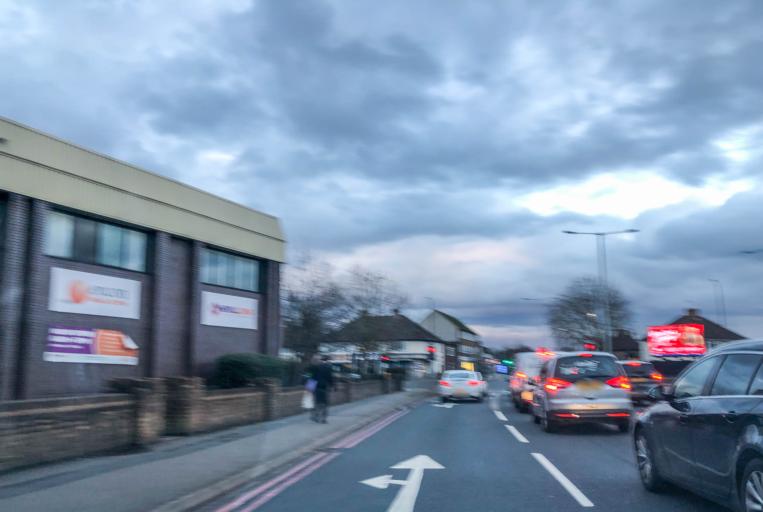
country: GB
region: England
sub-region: Greater London
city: Feltham
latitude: 51.4580
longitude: -0.4108
